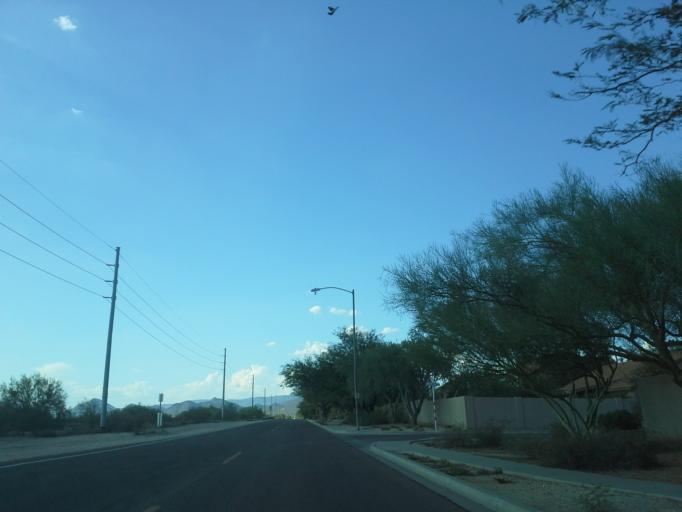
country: US
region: Arizona
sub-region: Maricopa County
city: Cave Creek
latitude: 33.7593
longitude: -111.9955
